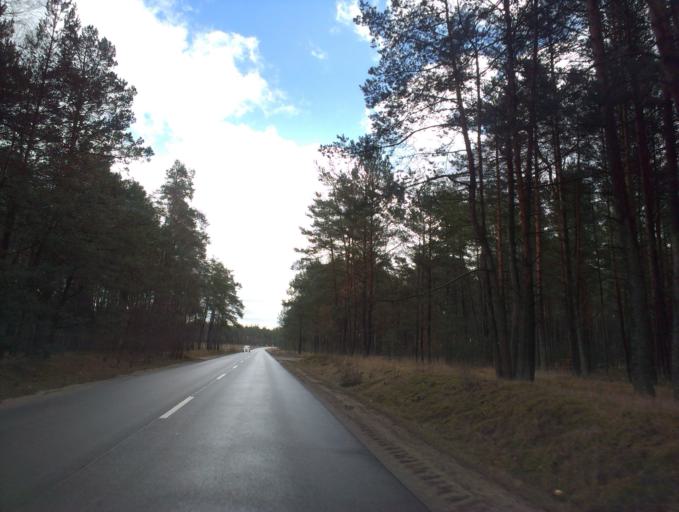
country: PL
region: Pomeranian Voivodeship
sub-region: Powiat czluchowski
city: Czarne
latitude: 53.6915
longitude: 16.9169
